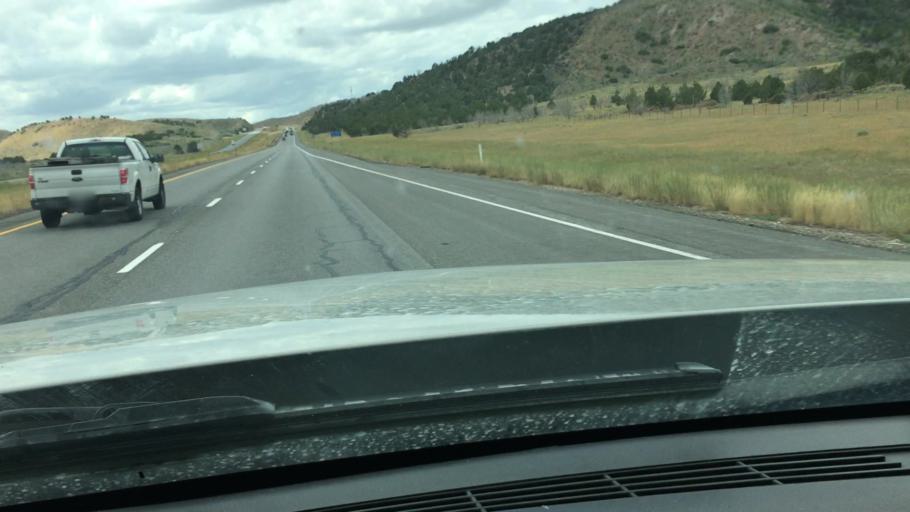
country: US
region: Utah
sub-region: Beaver County
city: Beaver
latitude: 38.6540
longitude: -112.5981
